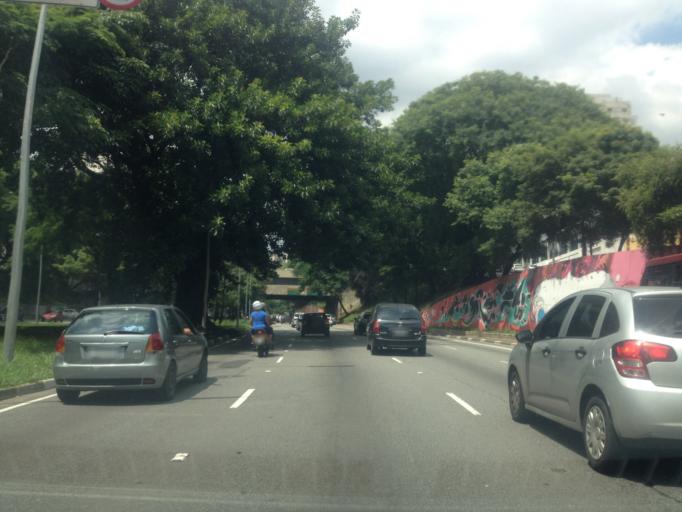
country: BR
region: Sao Paulo
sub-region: Sao Paulo
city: Sao Paulo
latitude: -23.5613
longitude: -46.6401
